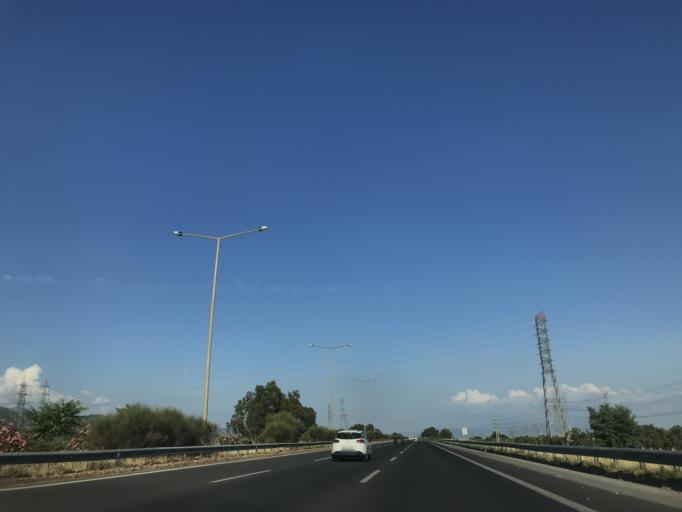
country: TR
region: Aydin
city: Germencik
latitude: 37.8746
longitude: 27.6183
